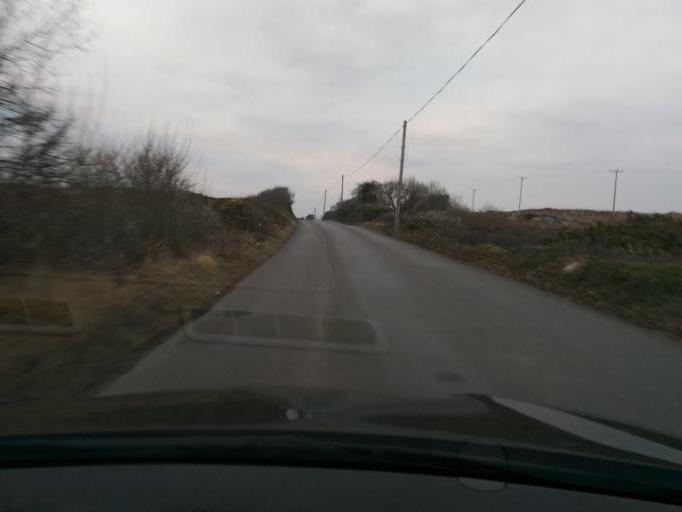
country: IE
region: Connaught
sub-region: County Galway
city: Bearna
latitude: 53.2719
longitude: -9.1596
